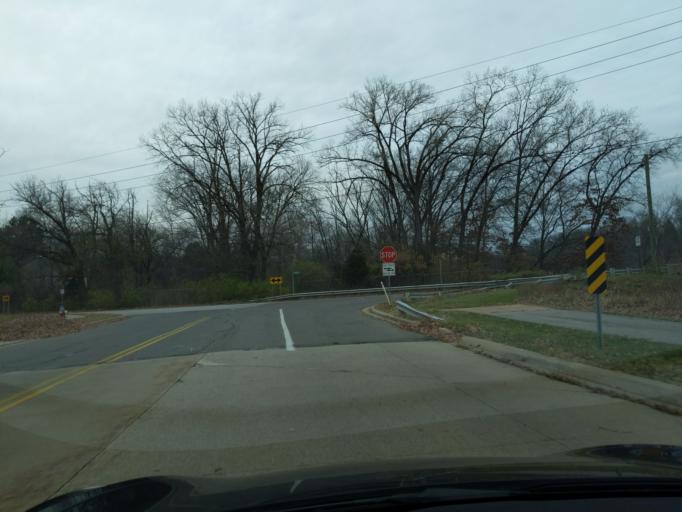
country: US
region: Indiana
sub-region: Saint Joseph County
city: Georgetown
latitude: 41.7301
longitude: -86.2700
